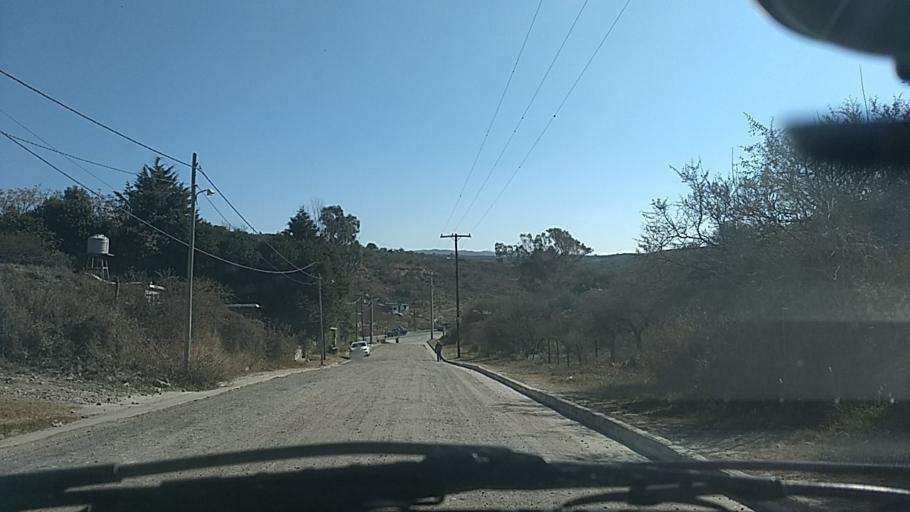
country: AR
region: Cordoba
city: Agua de Oro
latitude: -31.1006
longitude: -64.2901
